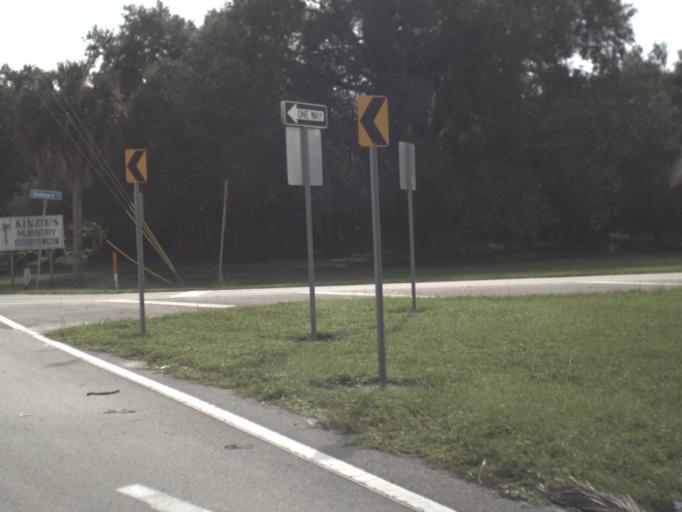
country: US
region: Florida
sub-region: Lee County
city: Fort Myers
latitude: 26.6472
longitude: -81.8562
